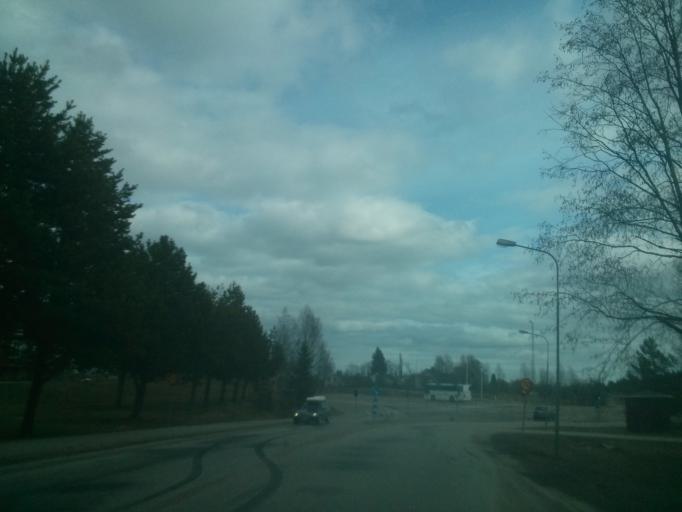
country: SE
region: Vaesternorrland
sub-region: Sundsvalls Kommun
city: Njurundabommen
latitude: 62.2731
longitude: 17.3734
